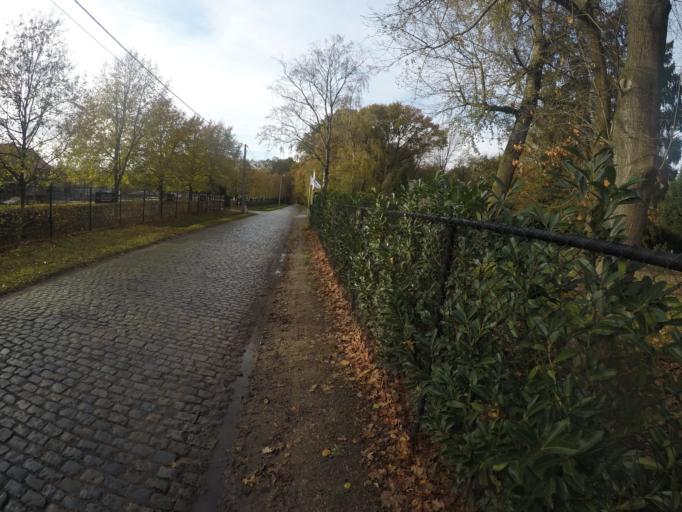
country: BE
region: Flanders
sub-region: Provincie Oost-Vlaanderen
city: Temse
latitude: 51.1685
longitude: 4.1950
